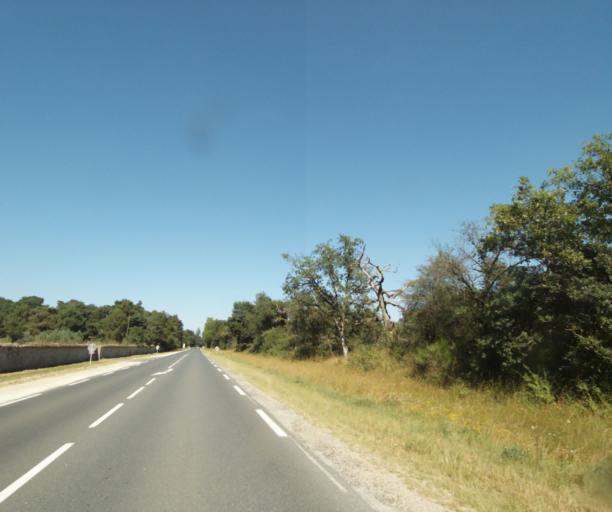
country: FR
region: Ile-de-France
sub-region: Departement de Seine-et-Marne
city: Fontainebleau
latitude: 48.3914
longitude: 2.6773
